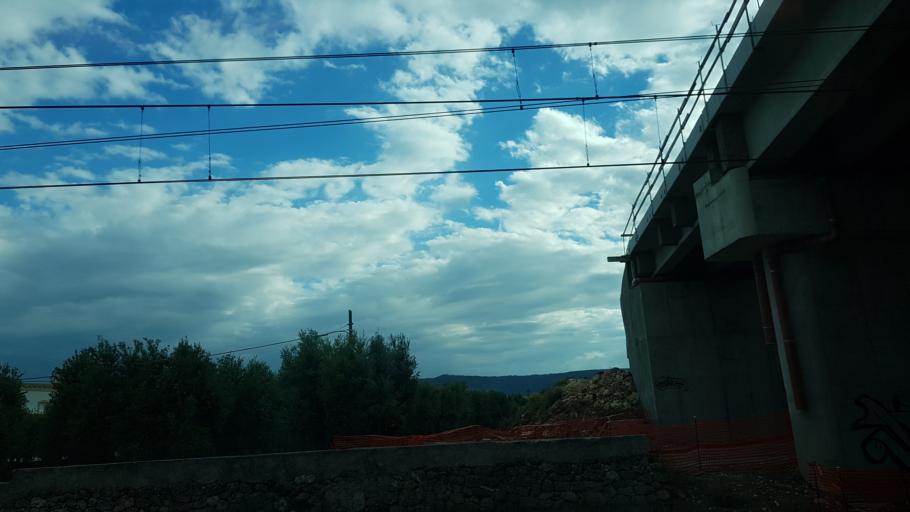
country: IT
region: Apulia
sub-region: Provincia di Brindisi
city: Montalbano
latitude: 40.8158
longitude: 17.4587
